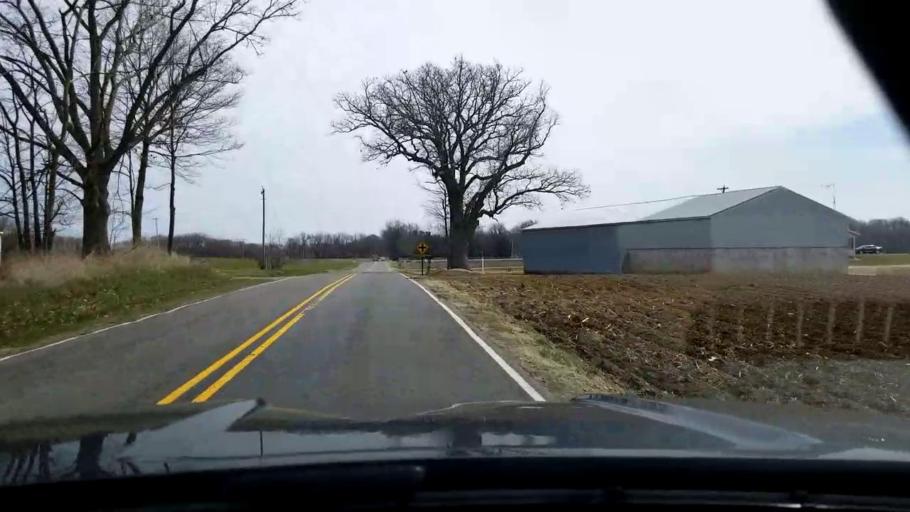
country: US
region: Michigan
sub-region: Jackson County
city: Spring Arbor
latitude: 42.1016
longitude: -84.5016
